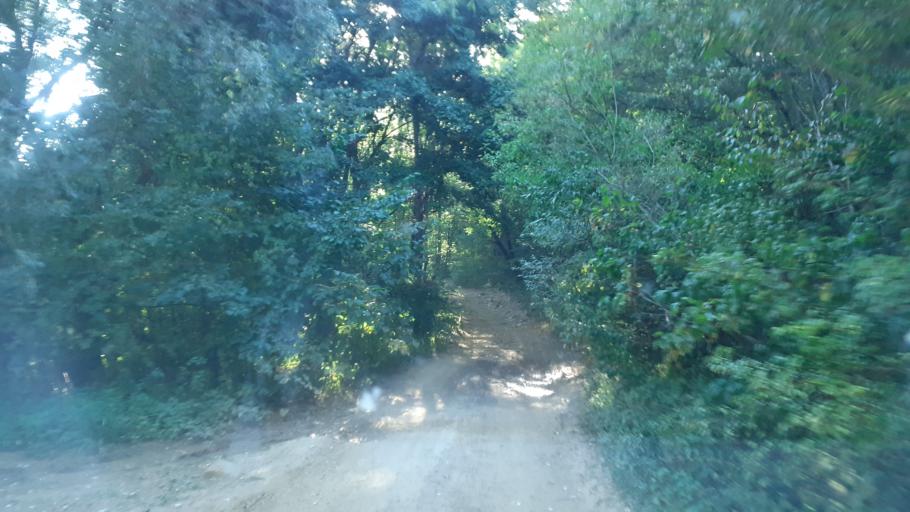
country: RU
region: Krasnodarskiy
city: Azovskaya
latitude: 44.6641
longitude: 38.4939
